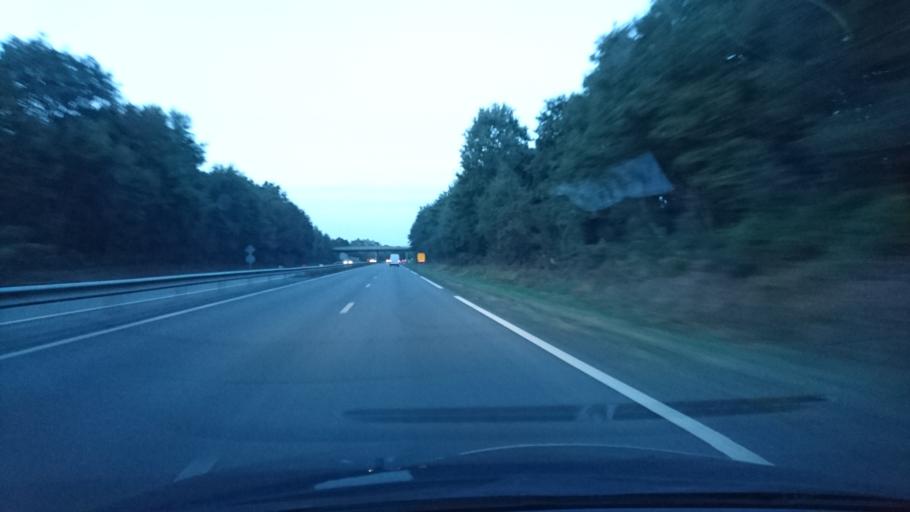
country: FR
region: Brittany
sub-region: Departement d'Ille-et-Vilaine
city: Bruz
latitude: 48.0425
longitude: -1.7553
